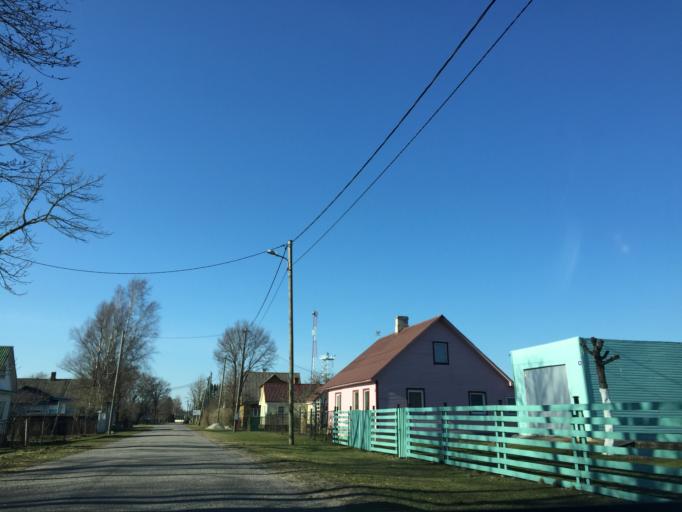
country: RU
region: Pskov
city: Gdov
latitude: 59.0010
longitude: 27.7392
